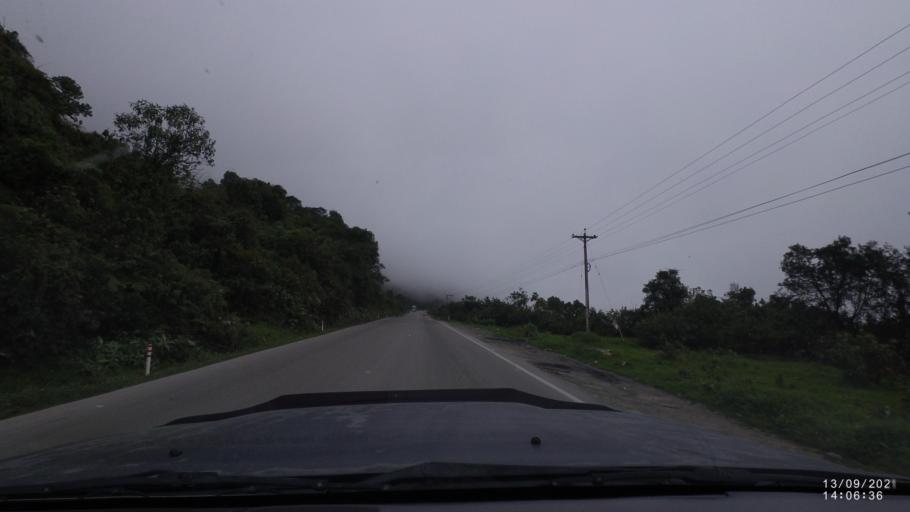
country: BO
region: Cochabamba
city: Colomi
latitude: -17.1866
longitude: -65.8838
